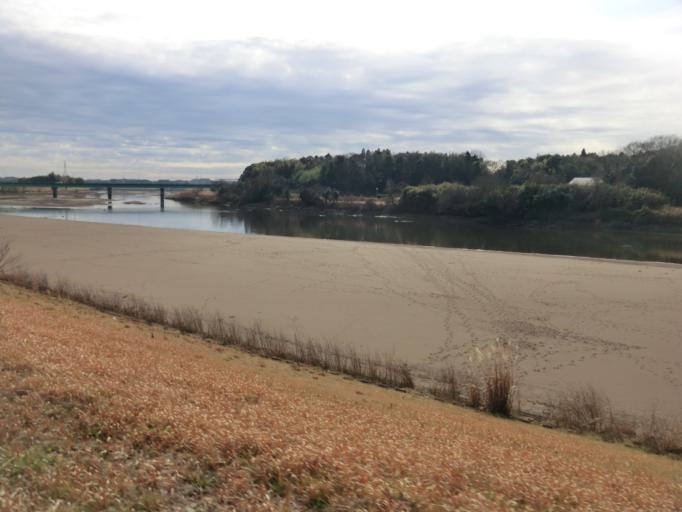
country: JP
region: Ibaraki
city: Moriya
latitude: 35.9504
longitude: 140.0259
